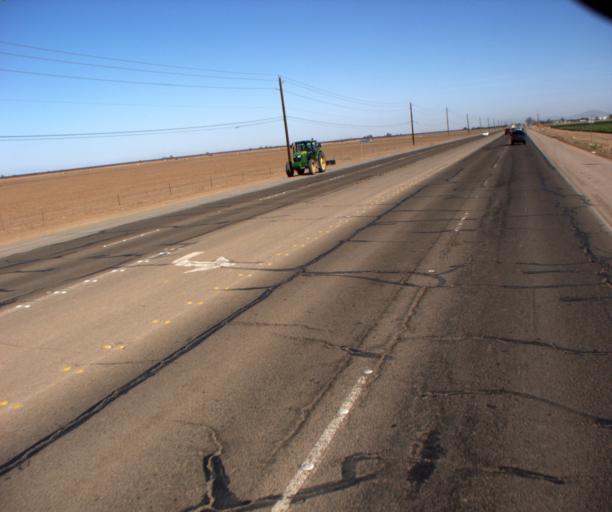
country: US
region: Arizona
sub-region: Yuma County
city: San Luis
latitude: 32.5309
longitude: -114.7867
